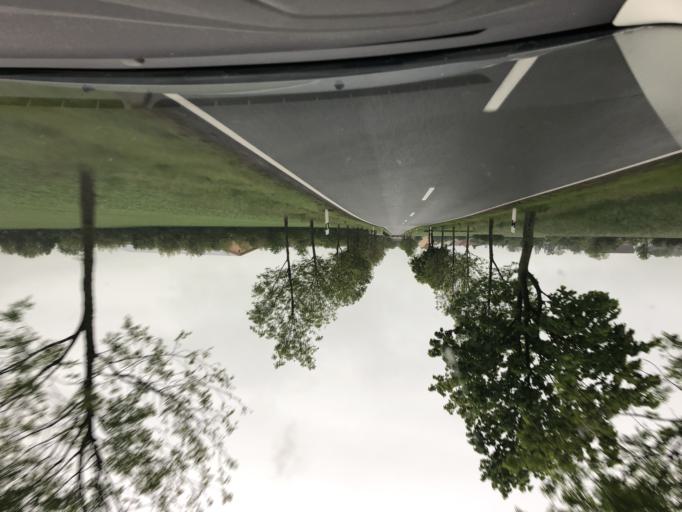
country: DE
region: Saxony
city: Krostitz
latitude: 51.4360
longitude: 12.5031
